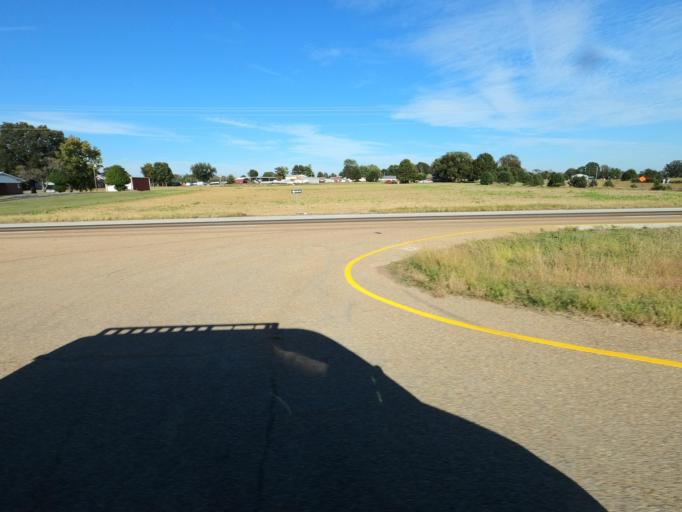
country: US
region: Tennessee
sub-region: Crockett County
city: Alamo
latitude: 35.8209
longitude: -89.1692
